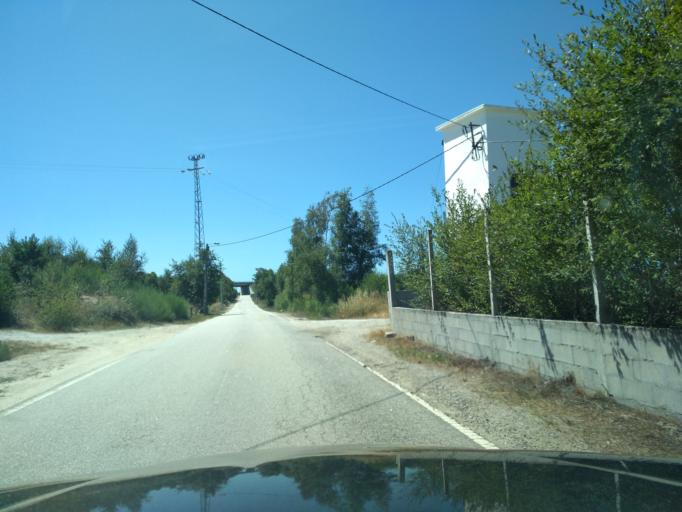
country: PT
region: Vila Real
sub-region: Vila Pouca de Aguiar
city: Vila Pouca de Aguiar
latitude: 41.4988
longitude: -7.6695
